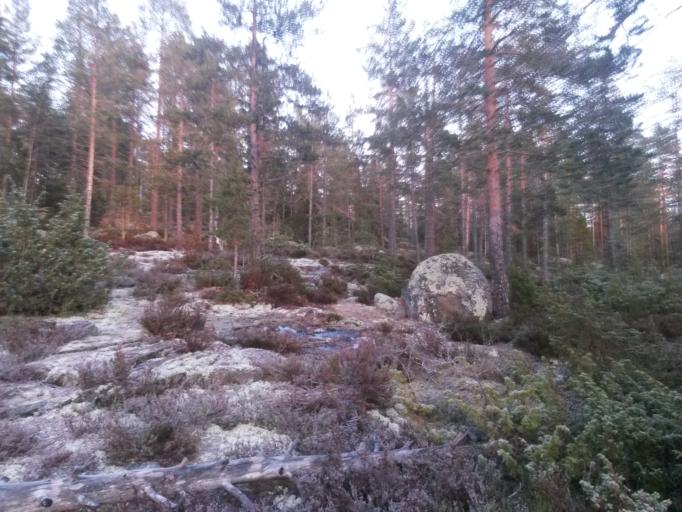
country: SE
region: Vaesterbotten
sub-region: Skelleftea Kommun
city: Soedra Bergsbyn
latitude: 64.7648
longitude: 21.0526
